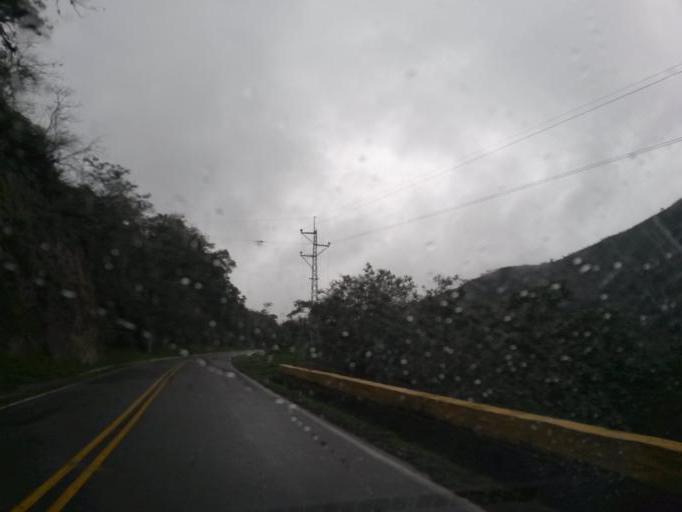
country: CO
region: Cauca
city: Popayan
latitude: 2.4024
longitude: -76.5015
